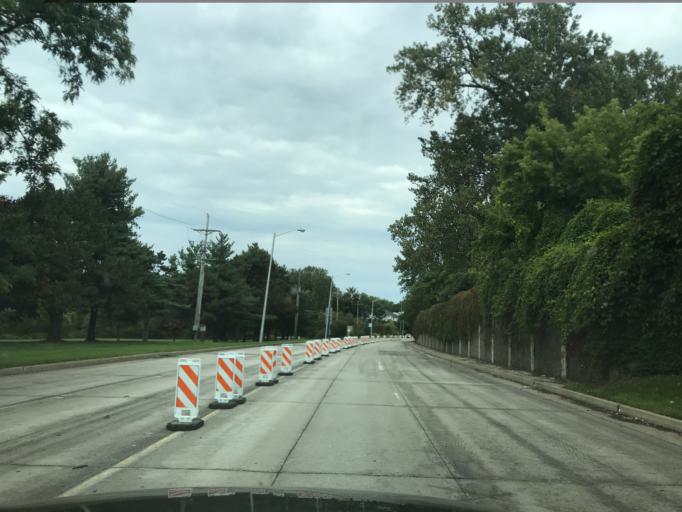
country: US
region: Pennsylvania
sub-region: Erie County
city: Erie
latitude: 42.1160
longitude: -80.1157
